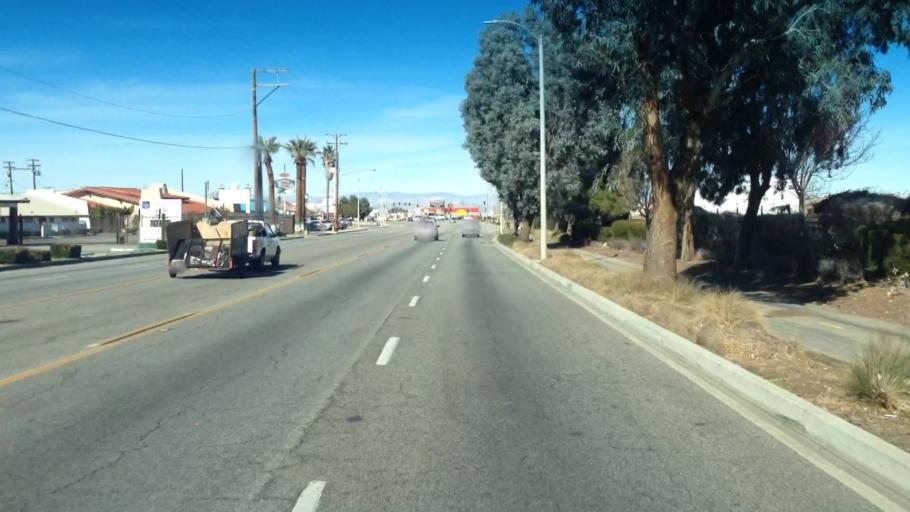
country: US
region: California
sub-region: Los Angeles County
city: Lancaster
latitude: 34.6861
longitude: -118.1346
